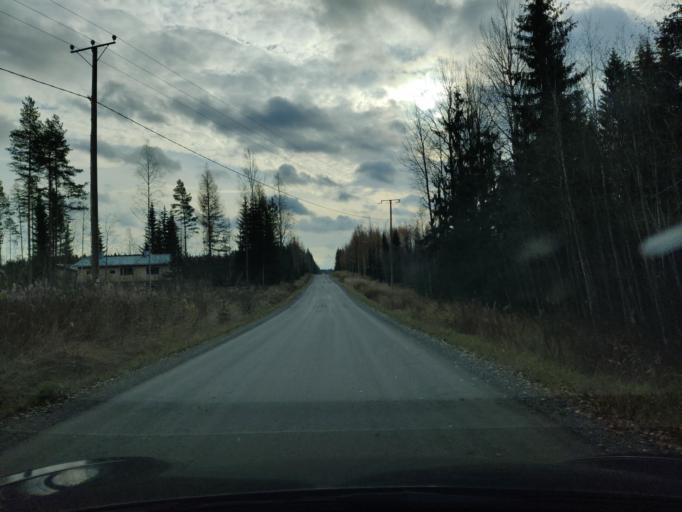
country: FI
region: Northern Savo
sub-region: Kuopio
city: Siilinjaervi
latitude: 63.1138
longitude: 27.5470
